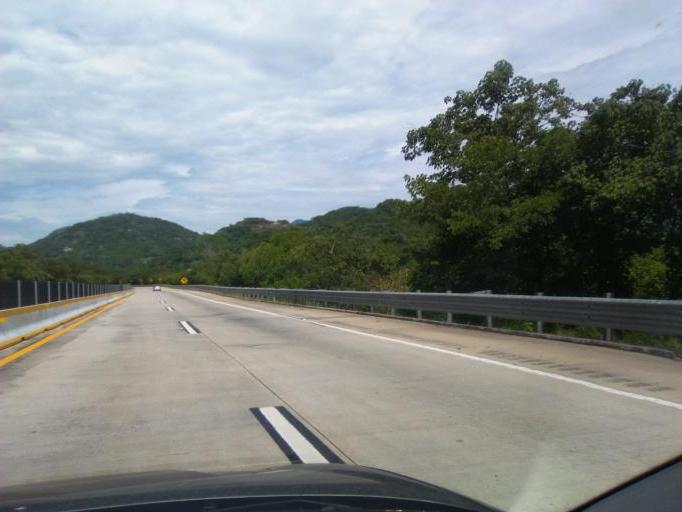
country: MX
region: Guerrero
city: Tierra Colorada
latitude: 17.1376
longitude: -99.5542
